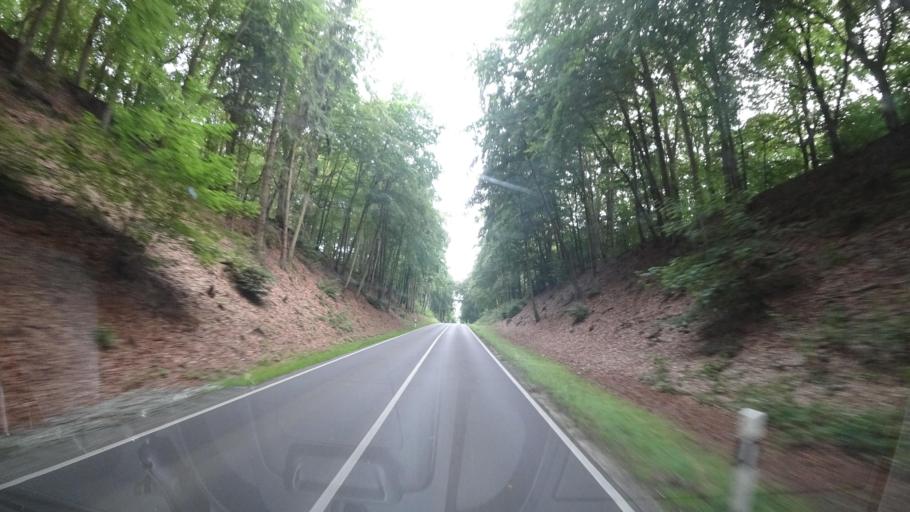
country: DE
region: Mecklenburg-Vorpommern
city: Ostseebad Binz
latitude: 54.4338
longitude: 13.5538
